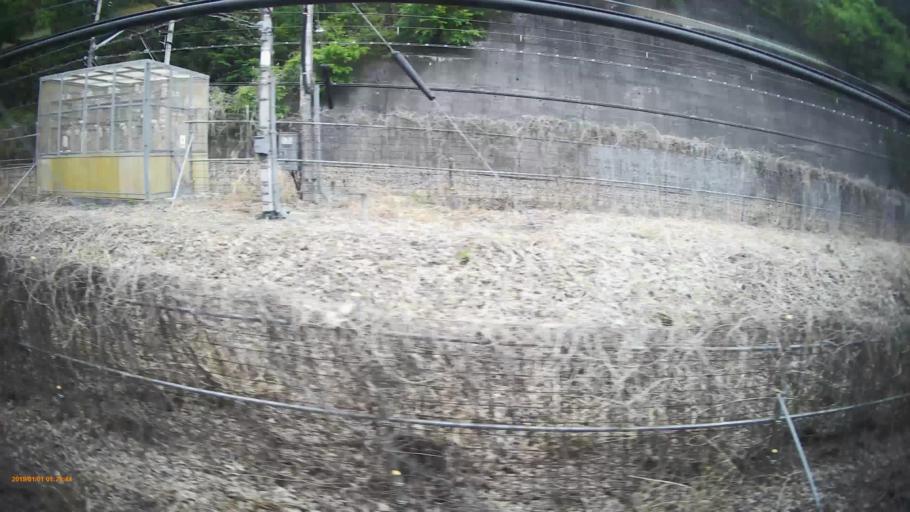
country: JP
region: Yamanashi
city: Enzan
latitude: 35.6884
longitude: 138.7423
